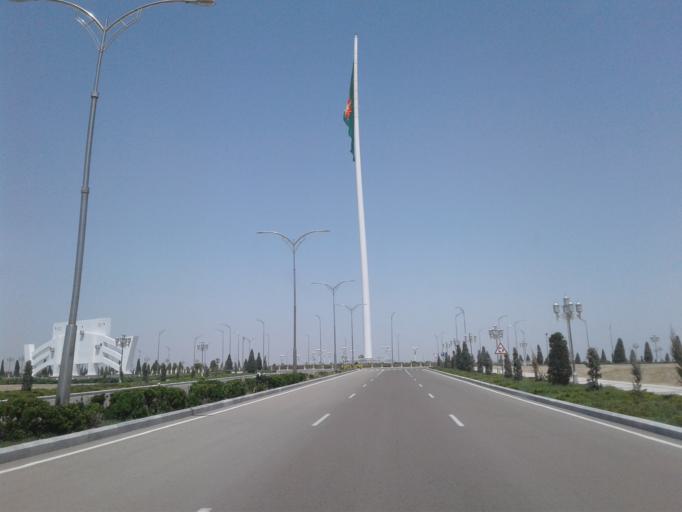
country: TM
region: Balkan
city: Turkmenbasy
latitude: 39.9581
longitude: 52.8622
